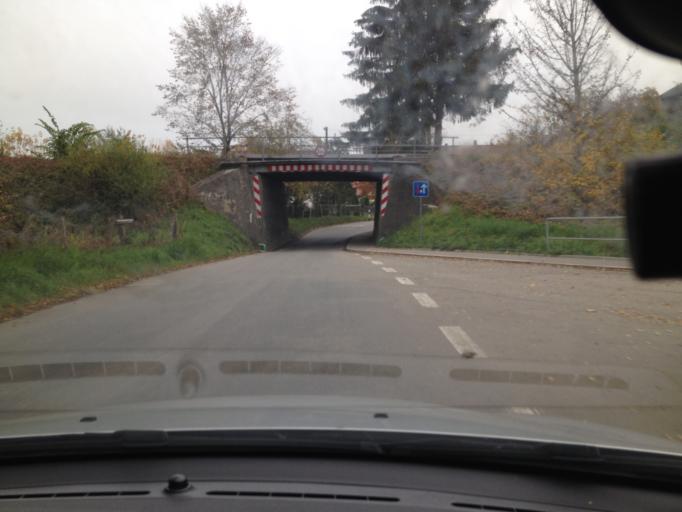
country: DE
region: Bavaria
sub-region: Swabia
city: Lamerdingen
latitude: 48.0937
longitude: 10.7313
